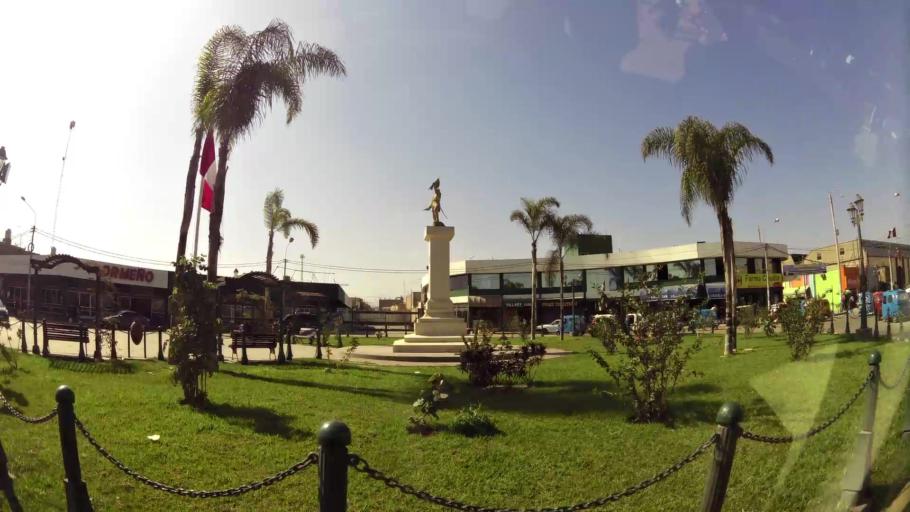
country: PE
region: Ica
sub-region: Provincia de Chincha
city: Chincha Alta
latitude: -13.4169
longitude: -76.1379
